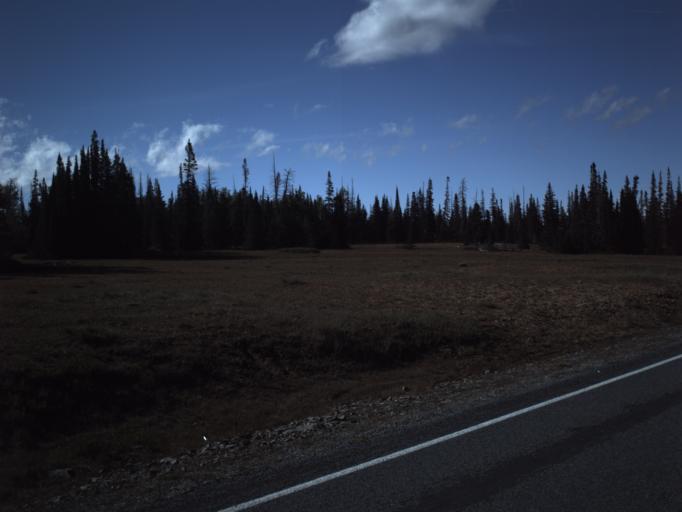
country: US
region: Utah
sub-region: Iron County
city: Parowan
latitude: 37.6698
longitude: -112.8398
